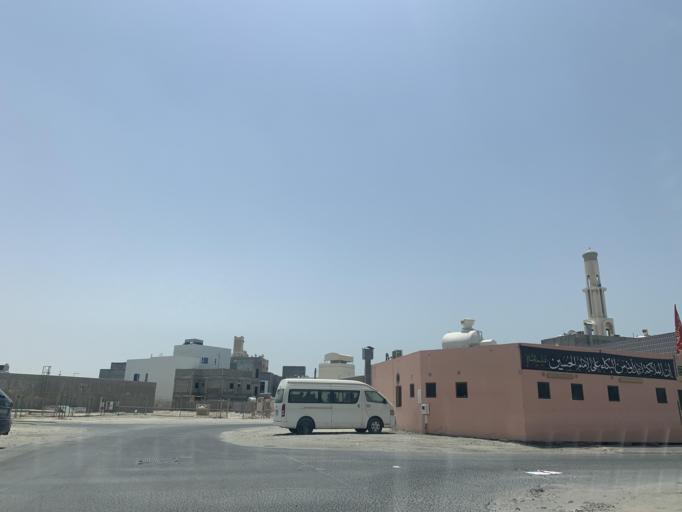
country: BH
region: Central Governorate
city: Madinat Hamad
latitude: 26.1448
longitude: 50.5014
